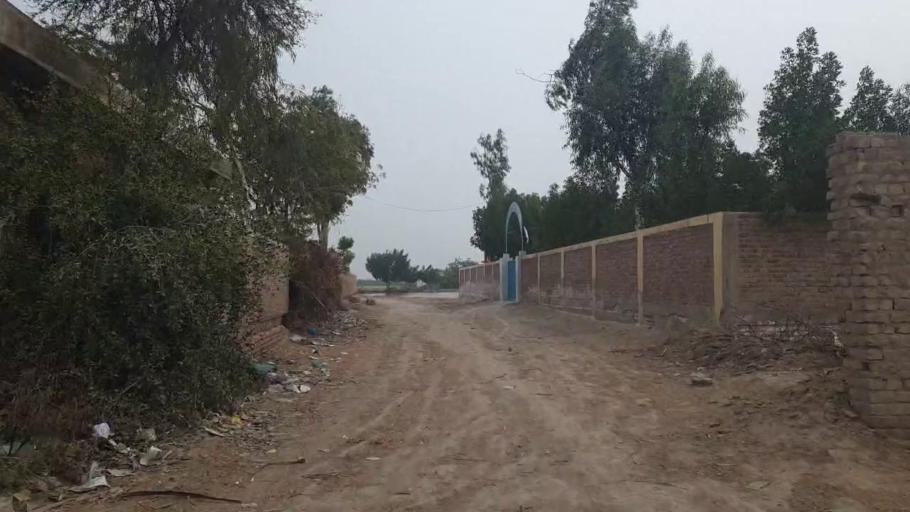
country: PK
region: Sindh
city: Tando Adam
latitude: 25.8202
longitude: 68.6561
